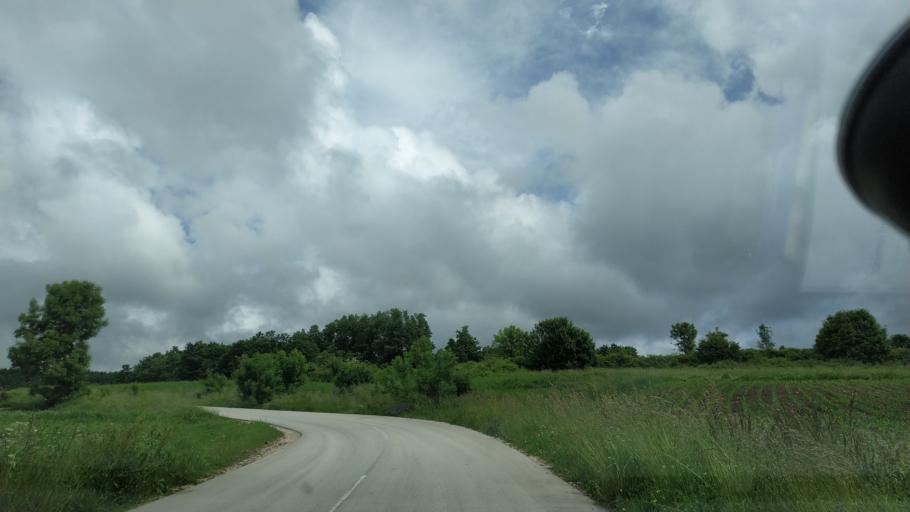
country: RS
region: Central Serbia
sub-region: Zajecarski Okrug
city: Soko Banja
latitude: 43.6853
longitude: 21.9314
